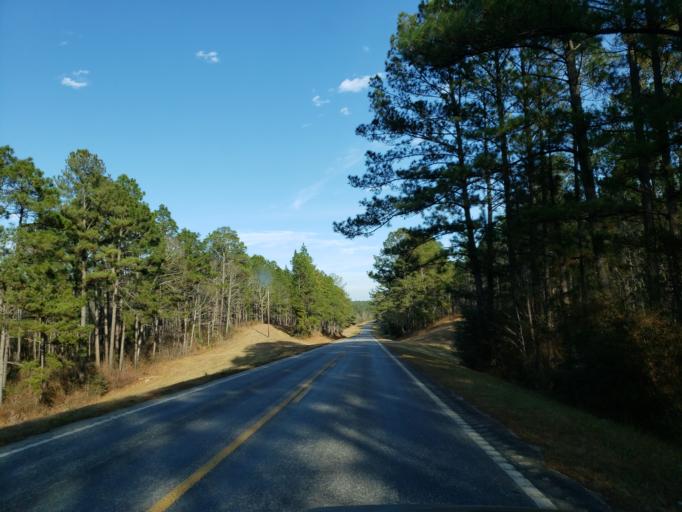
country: US
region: Mississippi
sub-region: Wayne County
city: Belmont
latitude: 31.3911
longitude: -88.6637
